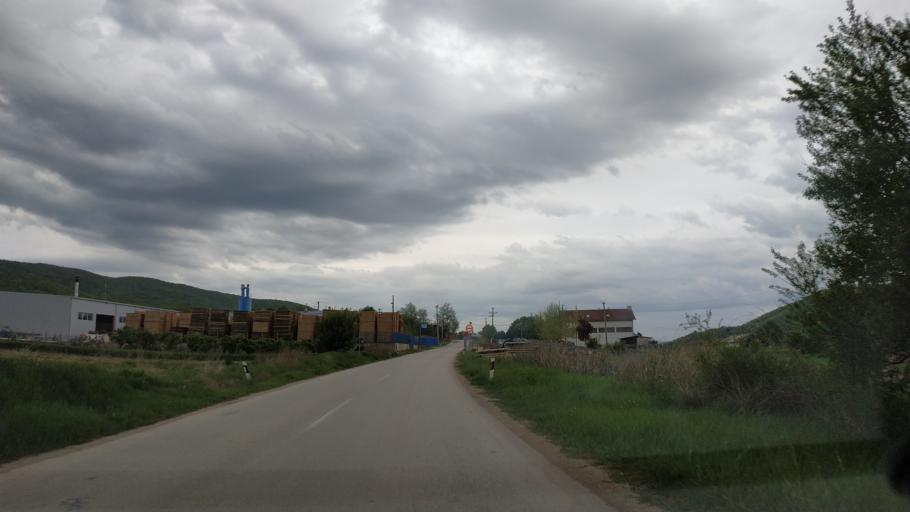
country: RS
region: Central Serbia
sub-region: Nisavski Okrug
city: Aleksinac
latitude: 43.5973
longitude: 21.6891
